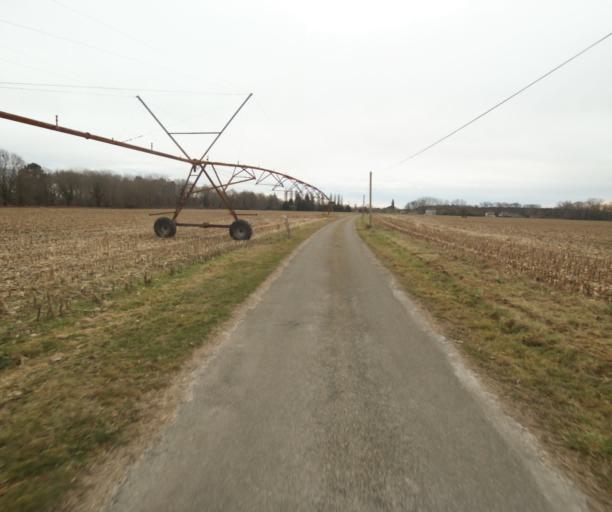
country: FR
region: Aquitaine
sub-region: Departement des Landes
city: Gabarret
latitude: 44.0102
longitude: -0.0320
